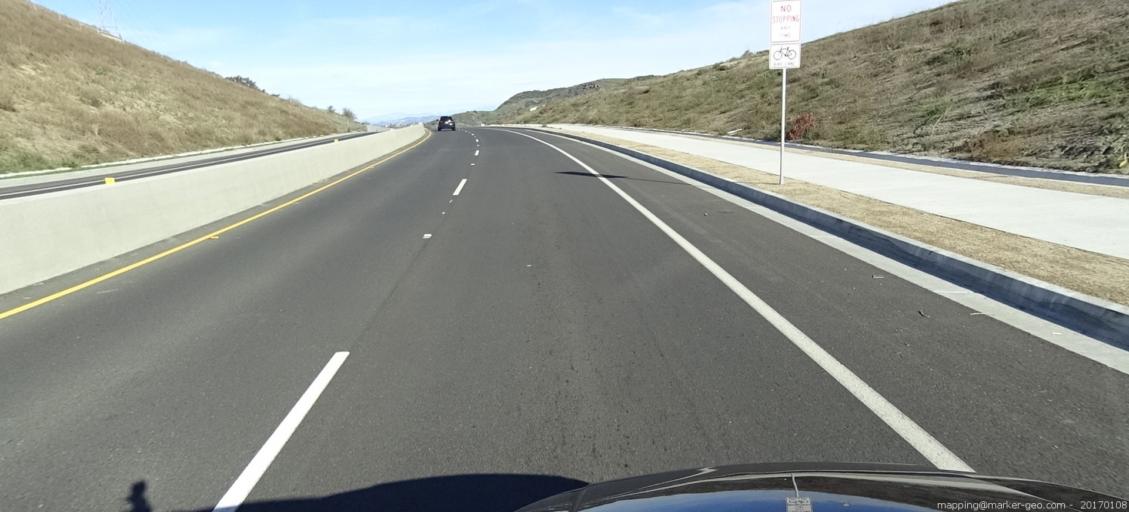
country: US
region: California
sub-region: Orange County
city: San Clemente
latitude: 33.4780
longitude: -117.6082
